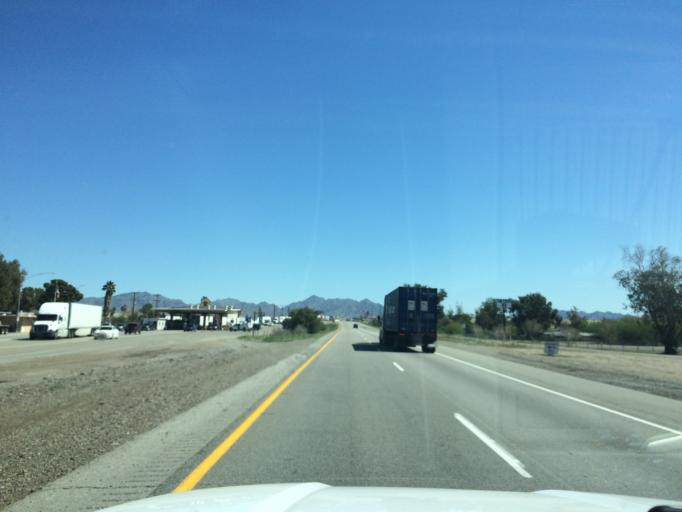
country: US
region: Arizona
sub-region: La Paz County
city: Ehrenberg
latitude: 33.6063
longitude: -114.5377
